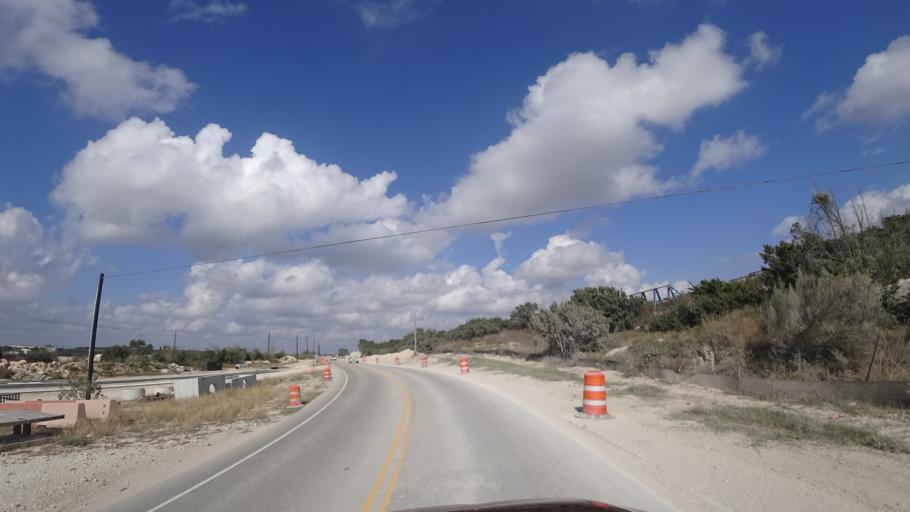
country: US
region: Texas
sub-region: Williamson County
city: Cedar Park
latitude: 30.5043
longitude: -97.8565
